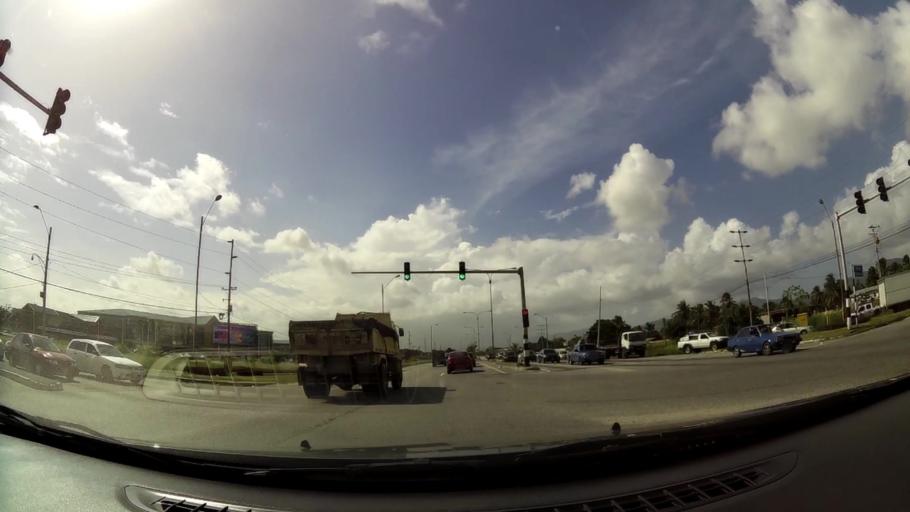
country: TT
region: Borough of Arima
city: Arima
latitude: 10.6096
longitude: -61.2909
